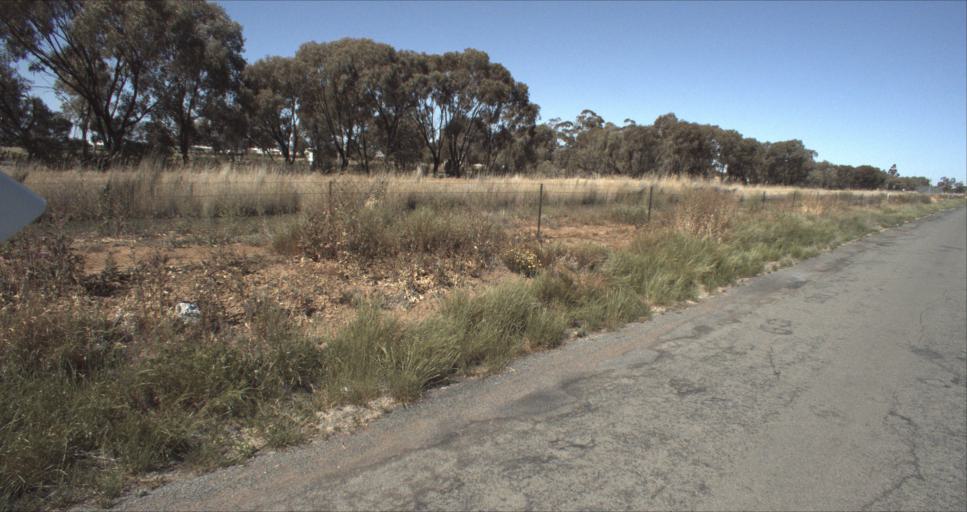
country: AU
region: New South Wales
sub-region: Leeton
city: Leeton
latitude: -34.5492
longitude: 146.3805
